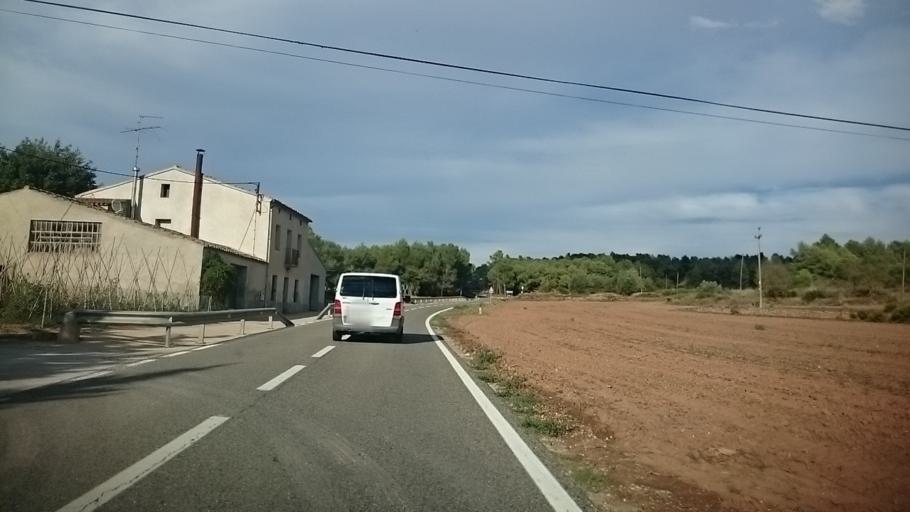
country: ES
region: Catalonia
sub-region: Provincia de Barcelona
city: Odena
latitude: 41.6238
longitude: 1.6580
